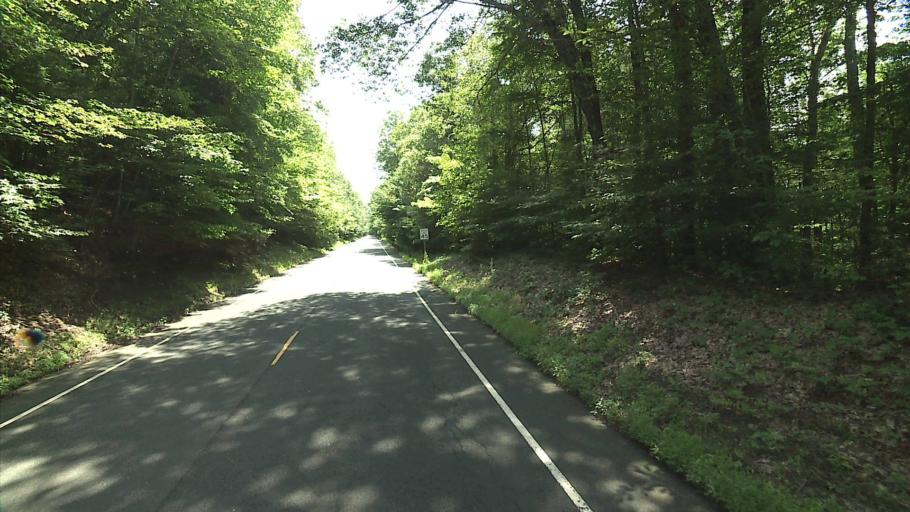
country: US
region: Massachusetts
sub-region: Hampden County
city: Granville
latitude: 42.0274
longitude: -72.9260
